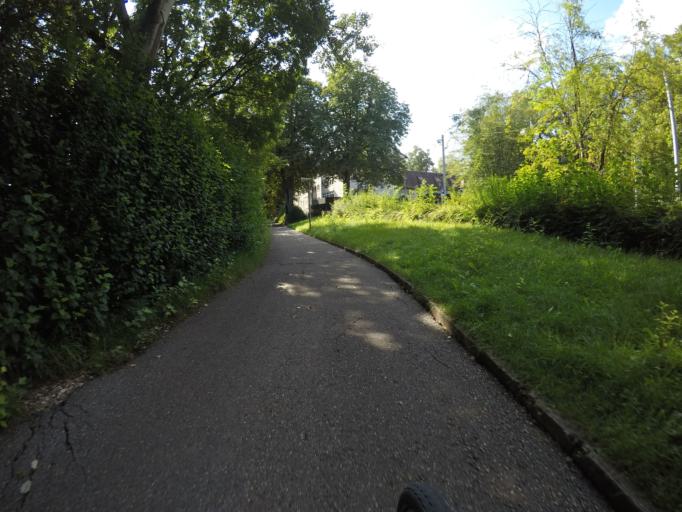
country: DE
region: Baden-Wuerttemberg
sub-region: Regierungsbezirk Stuttgart
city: Nurtingen
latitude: 48.6315
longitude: 9.3312
